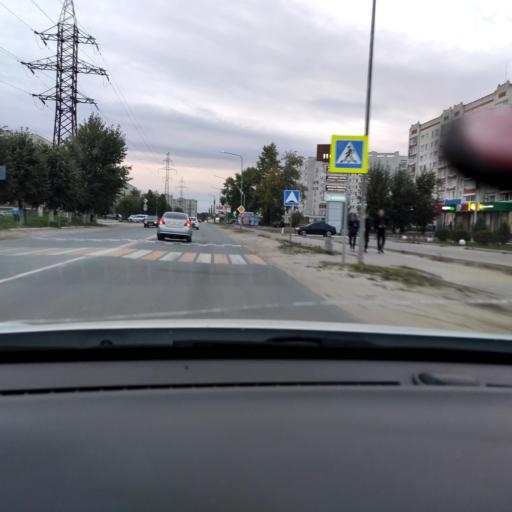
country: RU
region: Mariy-El
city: Volzhsk
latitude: 55.8660
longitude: 48.3569
